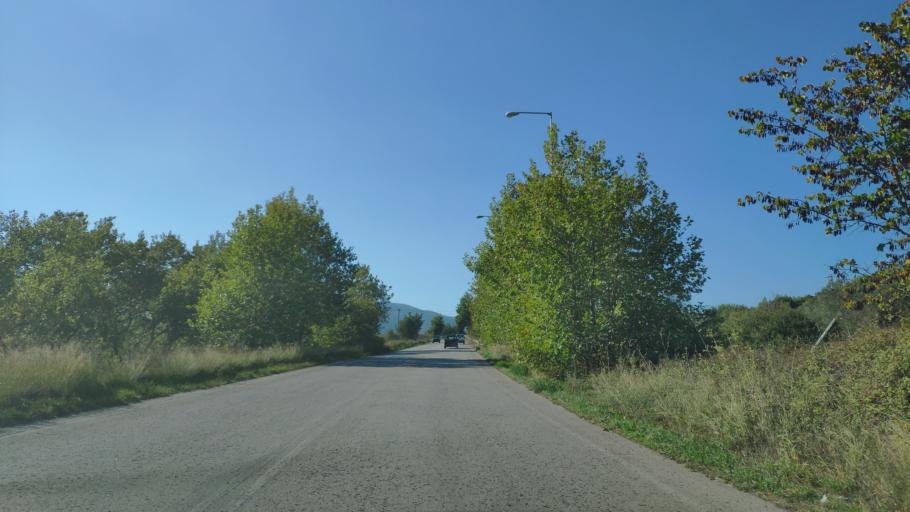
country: GR
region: Peloponnese
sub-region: Nomos Korinthias
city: Khiliomodhi
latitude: 37.8267
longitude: 22.8850
